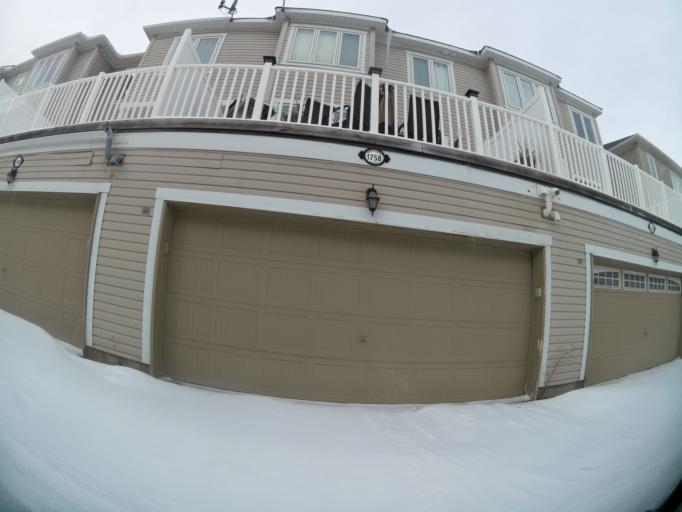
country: CA
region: Ontario
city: Bells Corners
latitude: 45.2893
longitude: -75.9190
